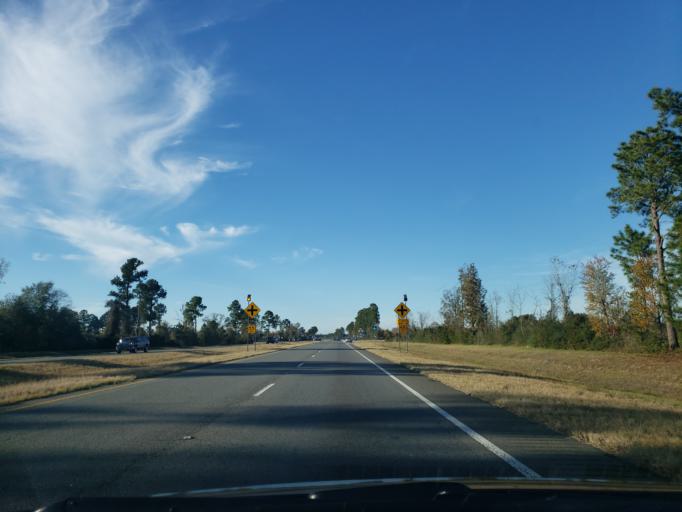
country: US
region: Georgia
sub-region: Ware County
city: Deenwood
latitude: 31.2408
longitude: -82.4288
